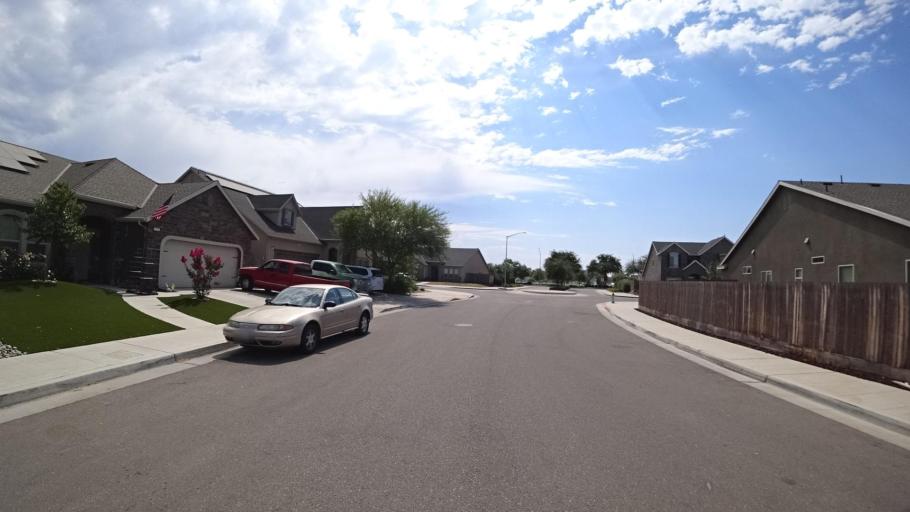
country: US
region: California
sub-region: Fresno County
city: Tarpey Village
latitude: 36.7843
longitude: -119.6691
